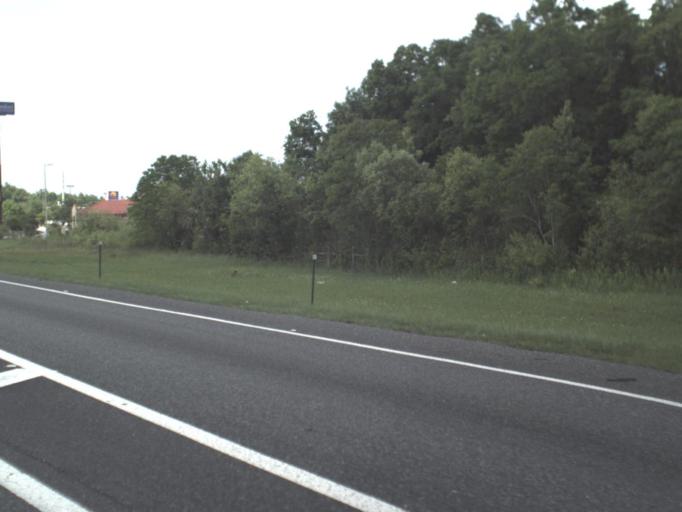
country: US
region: Florida
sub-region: Saint Johns County
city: Saint Augustine
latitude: 29.9136
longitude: -81.4107
